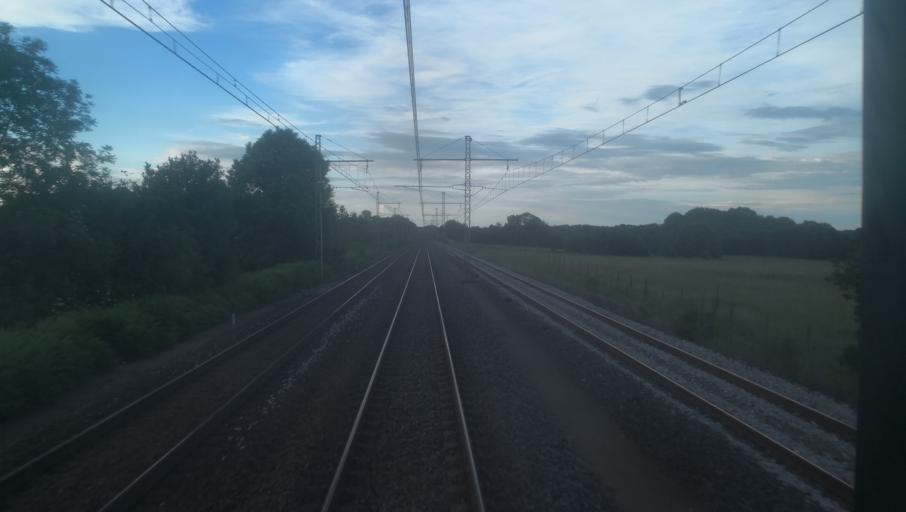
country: FR
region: Limousin
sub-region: Departement de la Creuse
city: Saint-Agnant-de-Versillat
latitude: 46.3177
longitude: 1.5241
